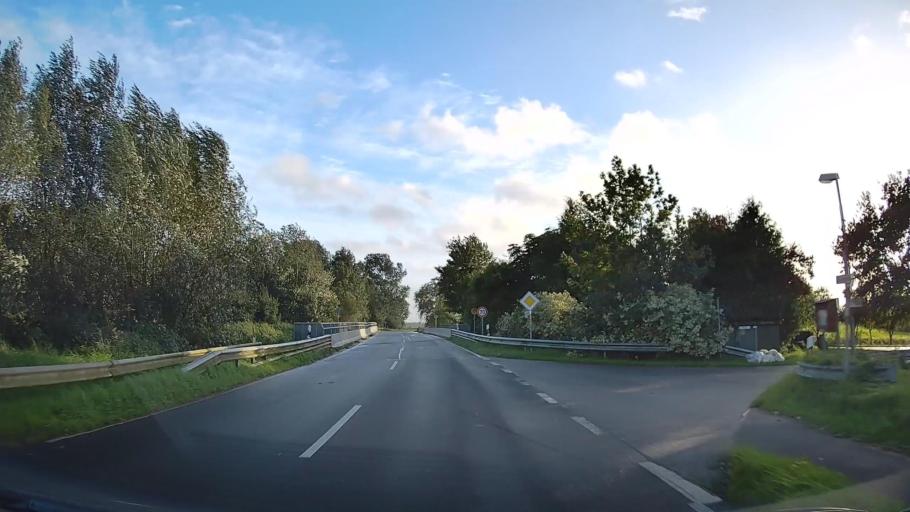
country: DE
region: Schleswig-Holstein
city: Sommerland
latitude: 53.8036
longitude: 9.5289
